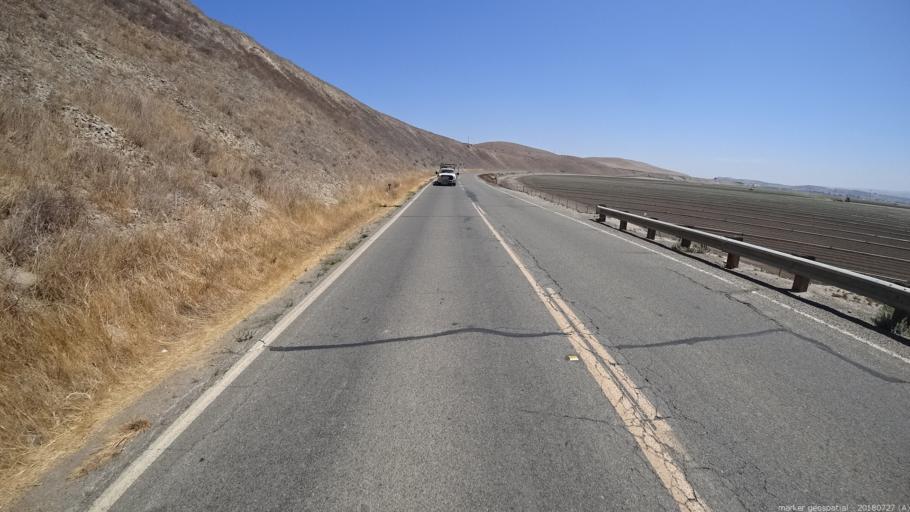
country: US
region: California
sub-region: Monterey County
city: King City
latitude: 36.1245
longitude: -121.0112
